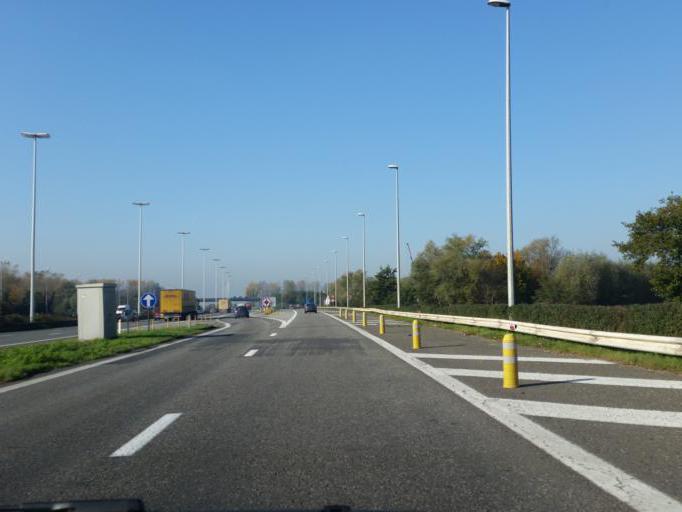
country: BE
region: Flanders
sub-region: Provincie West-Vlaanderen
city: Jabbeke
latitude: 51.1893
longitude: 3.0990
